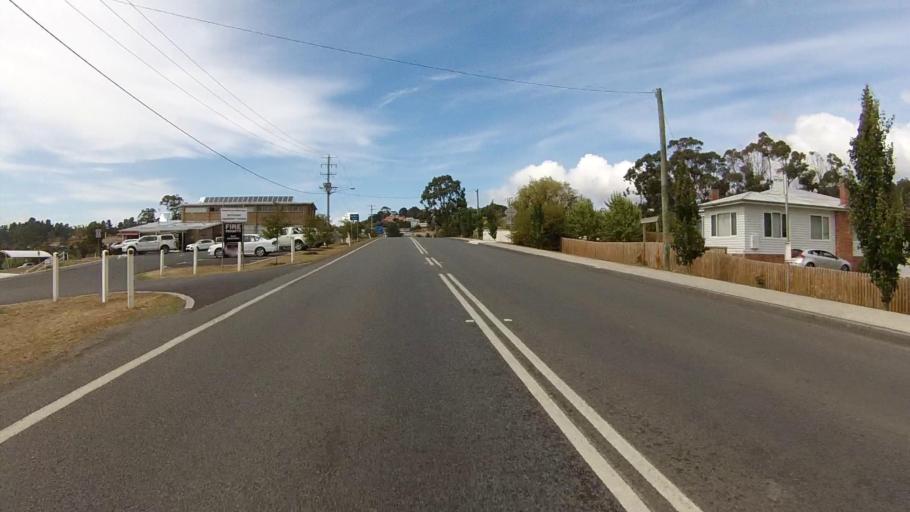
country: AU
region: Tasmania
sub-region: Kingborough
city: Kettering
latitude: -43.1245
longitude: 147.2454
